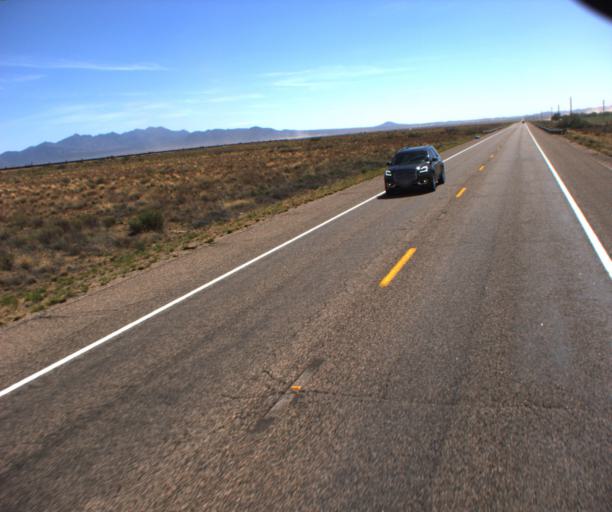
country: US
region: Arizona
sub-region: Mohave County
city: New Kingman-Butler
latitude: 35.3560
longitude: -113.8779
